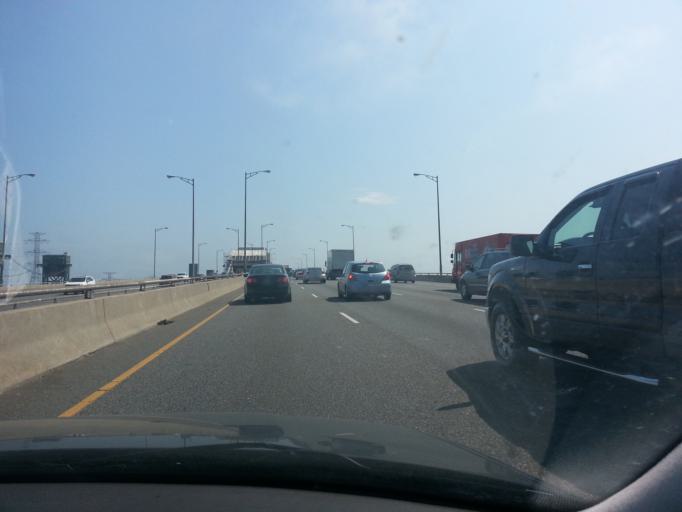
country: CA
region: Ontario
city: Hamilton
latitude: 43.3018
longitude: -79.7993
